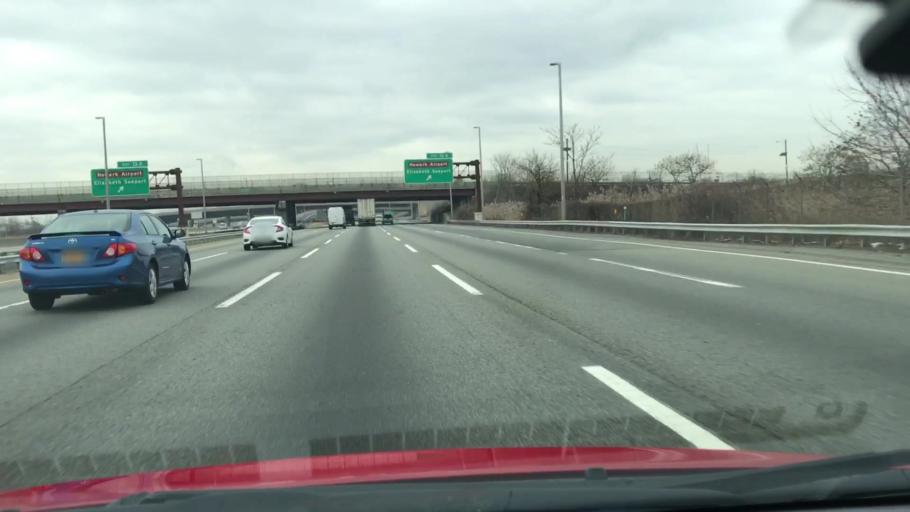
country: US
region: New Jersey
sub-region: Union County
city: Elizabeth
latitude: 40.6710
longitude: -74.1773
